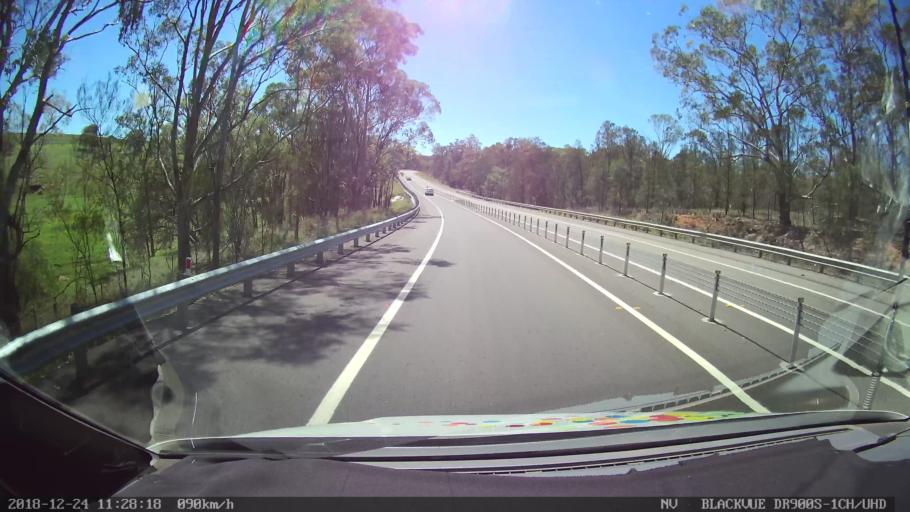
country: AU
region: New South Wales
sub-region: Upper Hunter Shire
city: Merriwa
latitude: -32.1887
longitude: 150.4453
